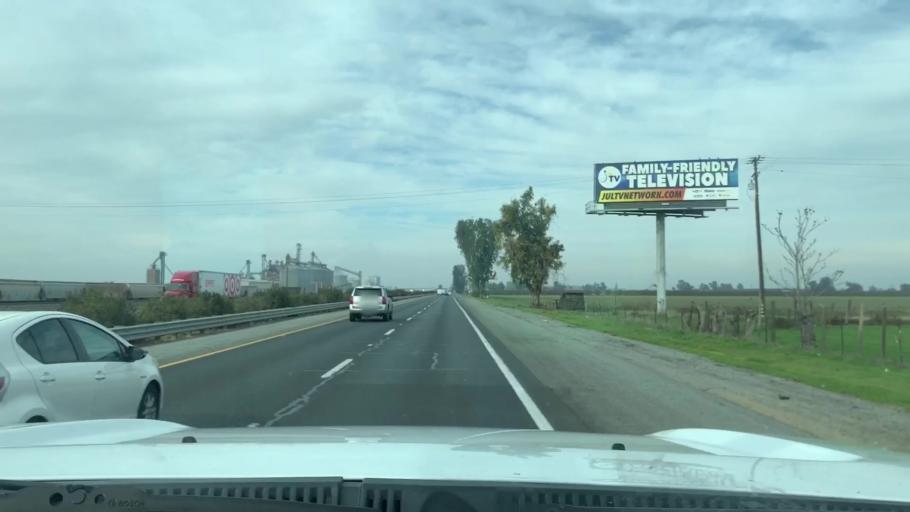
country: US
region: California
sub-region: Tulare County
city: Pixley
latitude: 35.9925
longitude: -119.2999
